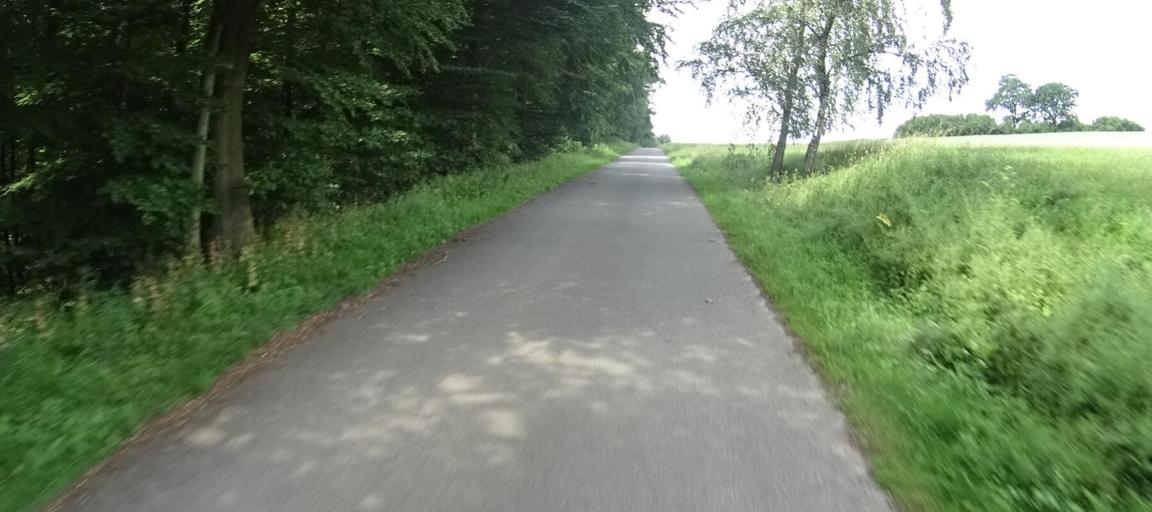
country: DE
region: Lower Saxony
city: Polle
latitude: 51.9125
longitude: 9.3903
